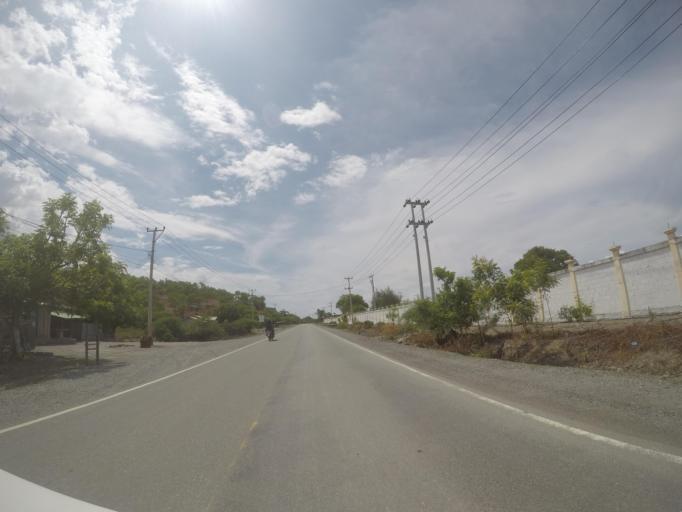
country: TL
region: Liquica
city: Liquica
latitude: -8.5643
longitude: 125.4123
